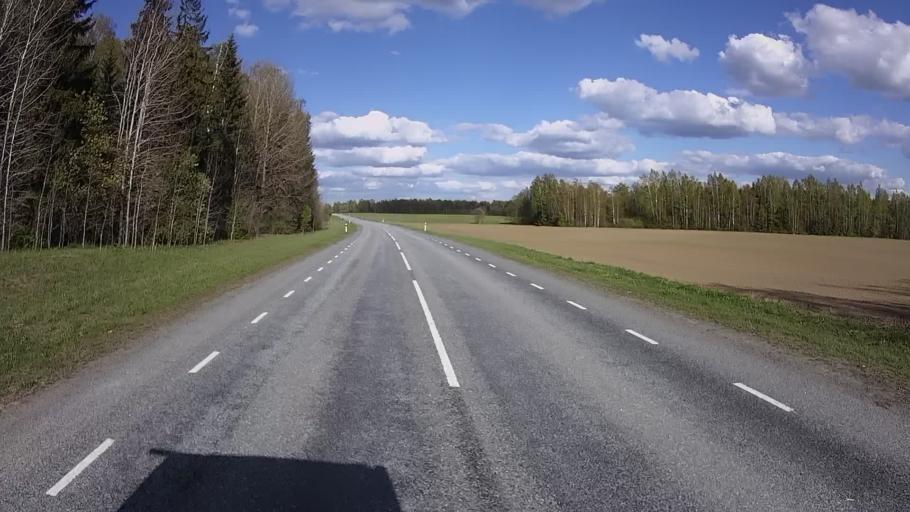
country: EE
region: Jogevamaa
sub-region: Poltsamaa linn
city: Poltsamaa
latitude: 58.6787
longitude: 26.0484
